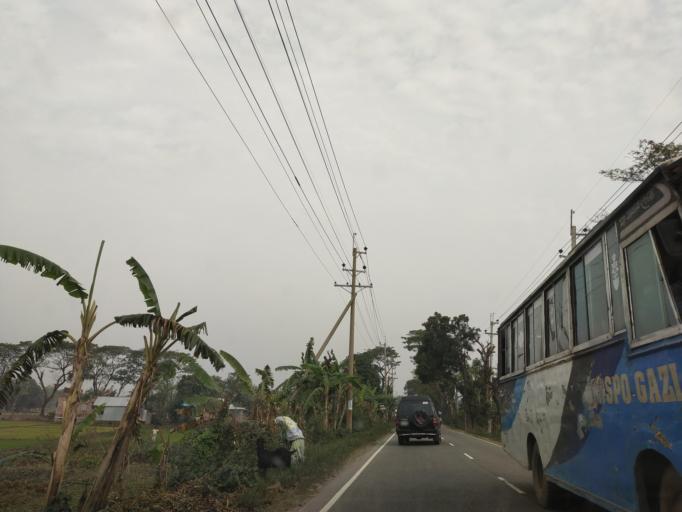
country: BD
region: Dhaka
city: Narsingdi
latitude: 23.9952
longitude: 90.7373
